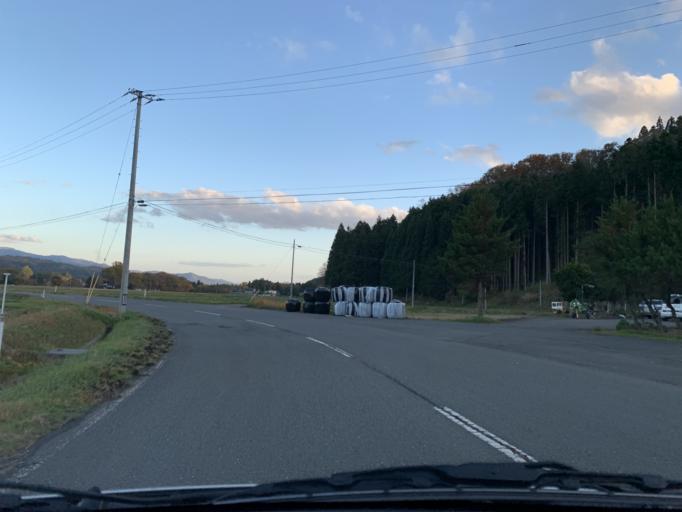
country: JP
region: Iwate
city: Mizusawa
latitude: 39.0401
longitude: 141.0519
